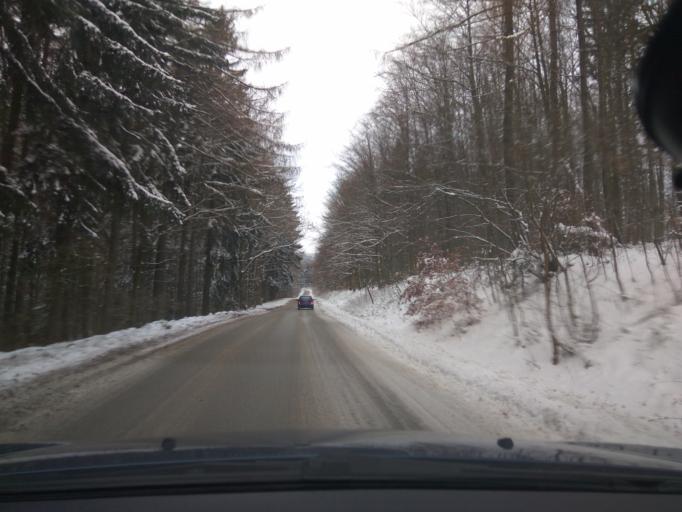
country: CZ
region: Zlin
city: Strani
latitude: 48.8475
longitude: 17.6901
